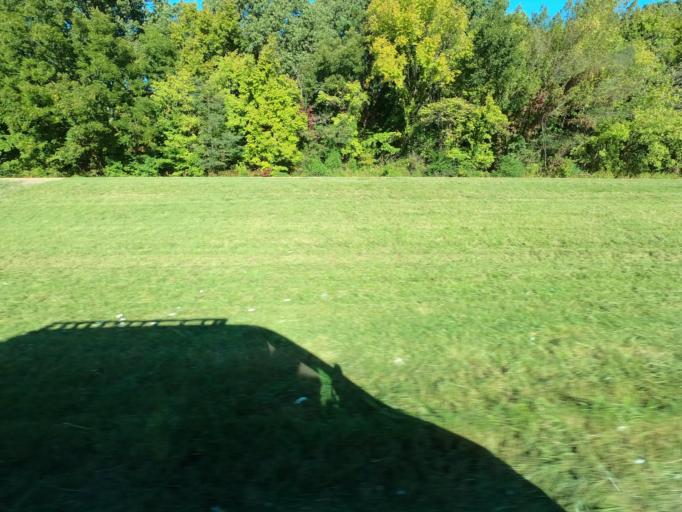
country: US
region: Tennessee
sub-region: Shelby County
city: Millington
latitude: 35.3851
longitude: -89.8610
